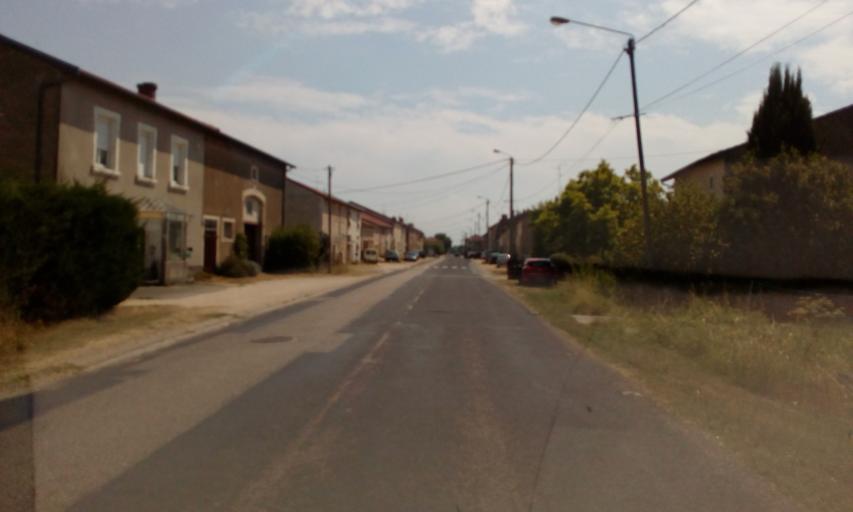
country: FR
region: Lorraine
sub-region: Departement de la Meuse
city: Vigneulles-les-Hattonchatel
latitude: 49.0407
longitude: 5.6551
